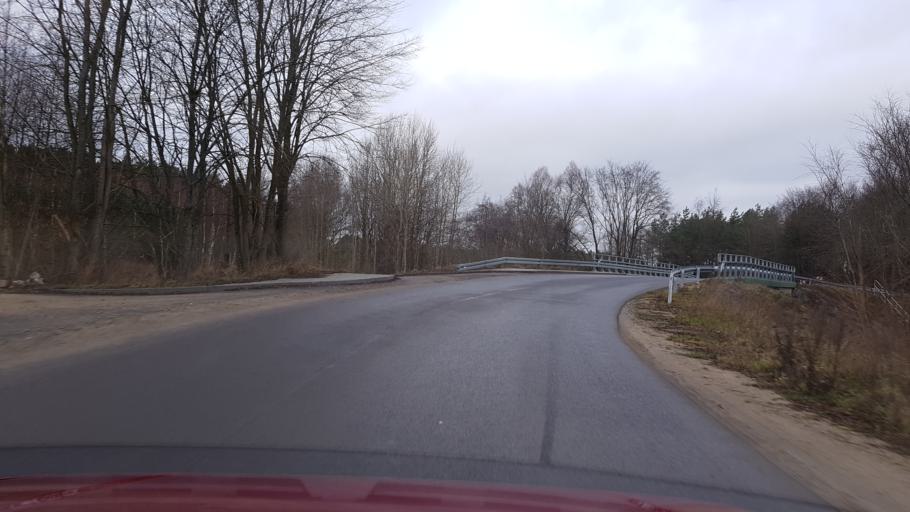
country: PL
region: Pomeranian Voivodeship
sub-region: Powiat bytowski
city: Borzytuchom
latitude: 54.1855
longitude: 17.3650
